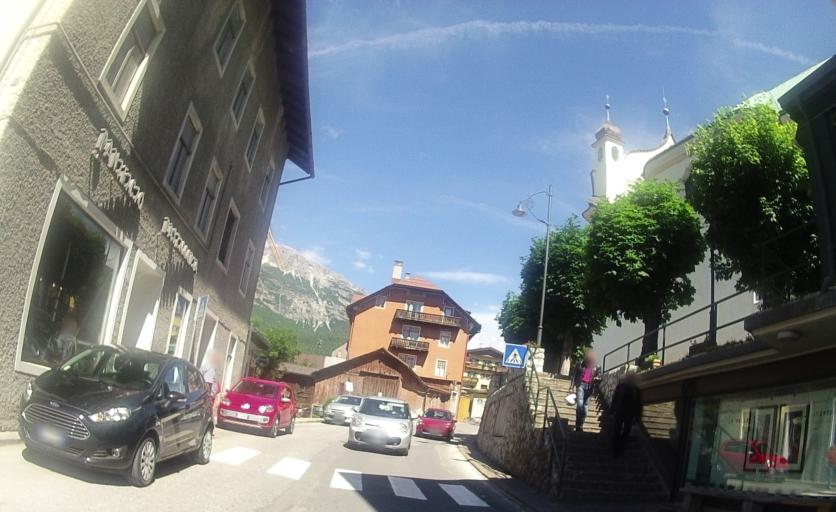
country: IT
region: Veneto
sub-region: Provincia di Belluno
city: Cortina d'Ampezzo
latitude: 46.5374
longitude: 12.1362
